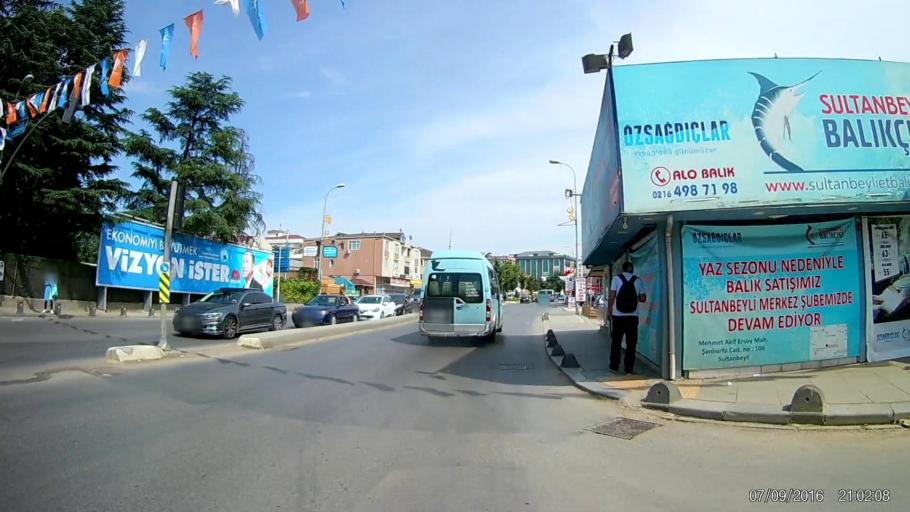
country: TR
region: Istanbul
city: Sultanbeyli
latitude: 40.9725
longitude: 29.2477
